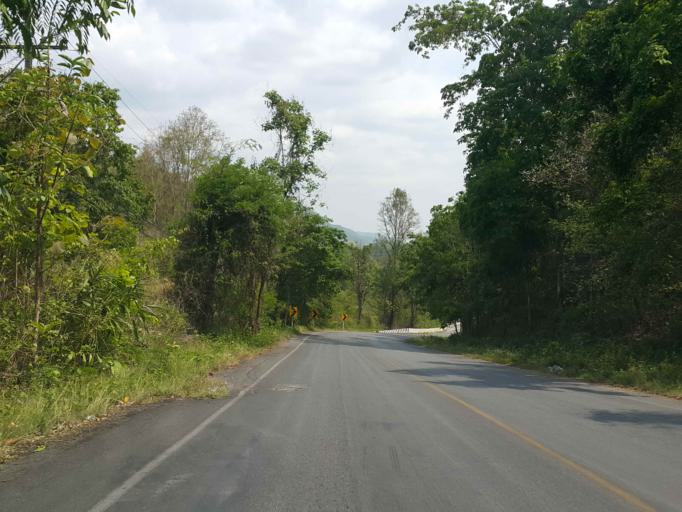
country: TH
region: Lampang
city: Thoen
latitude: 17.6122
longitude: 99.3252
